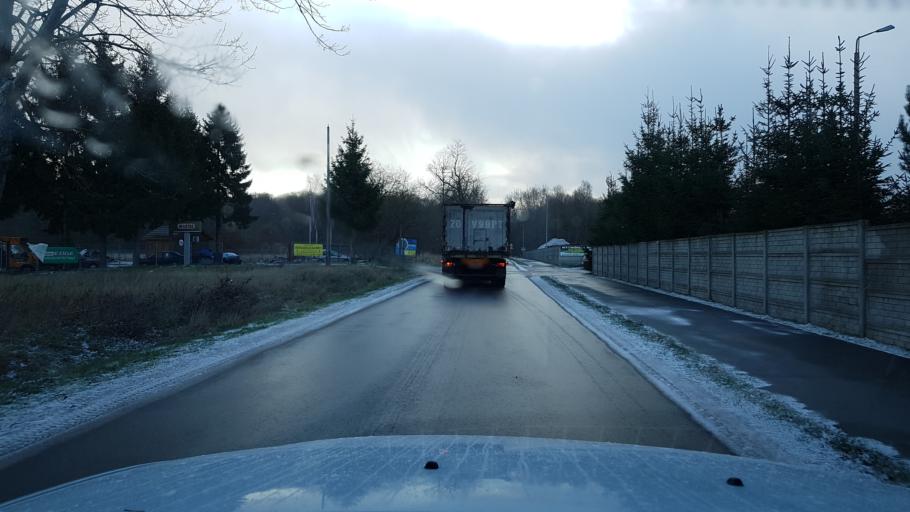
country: PL
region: West Pomeranian Voivodeship
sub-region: Powiat gryficki
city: Trzebiatow
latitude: 54.0507
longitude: 15.3083
